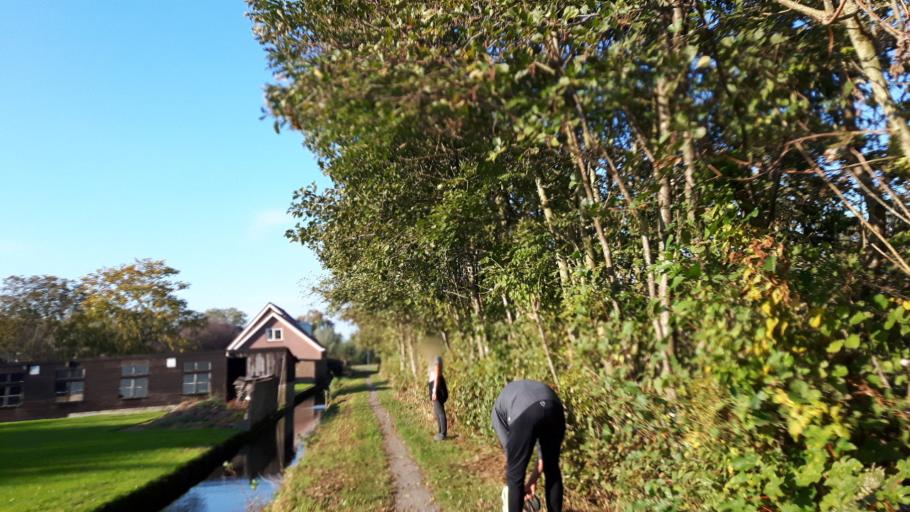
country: NL
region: Utrecht
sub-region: Gemeente Oudewater
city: Oudewater
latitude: 51.9868
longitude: 4.8821
